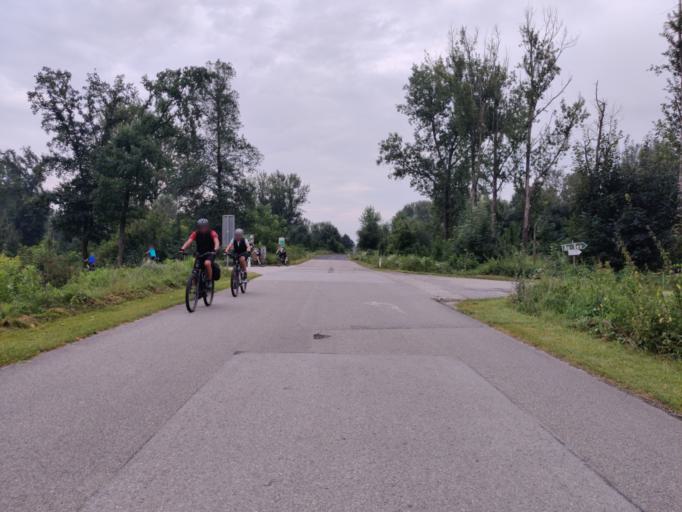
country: AT
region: Upper Austria
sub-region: Politischer Bezirk Linz-Land
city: Asten
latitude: 48.2356
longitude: 14.4241
